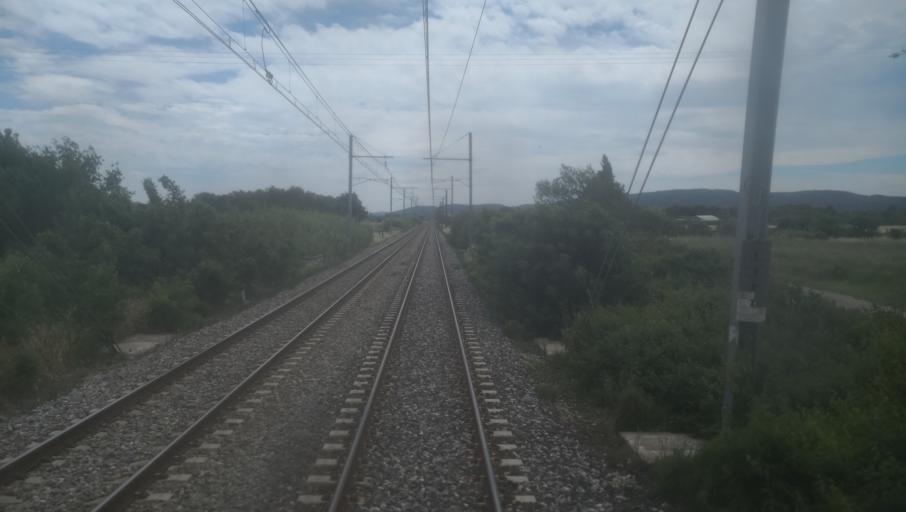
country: FR
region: Languedoc-Roussillon
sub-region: Departement de l'Herault
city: Mireval
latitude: 43.5152
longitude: 3.8191
